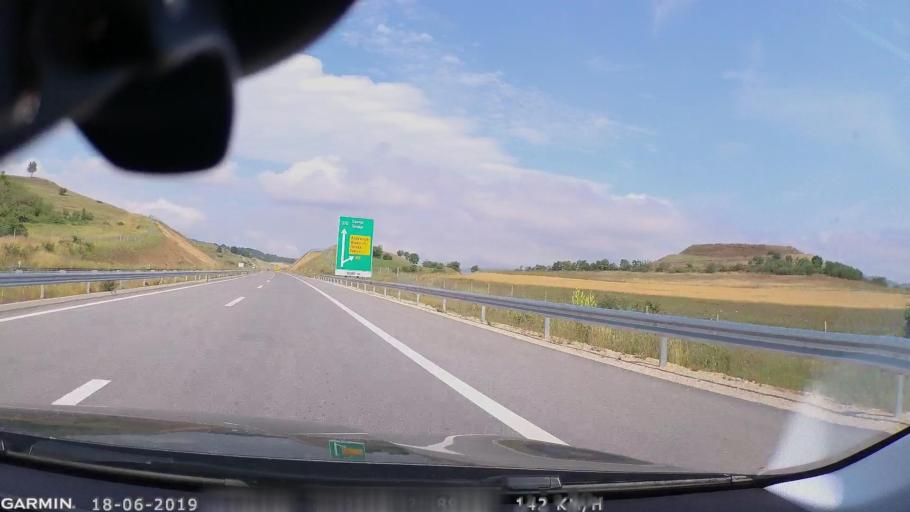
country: MK
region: Sveti Nikole
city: Gorobinci
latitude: 41.9129
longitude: 21.8944
